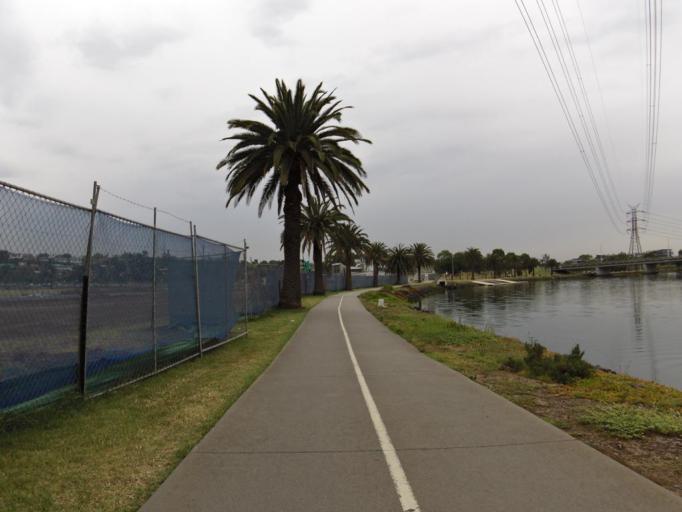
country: AU
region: Victoria
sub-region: Maribyrnong
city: Footscray
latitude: -37.7920
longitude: 144.9037
